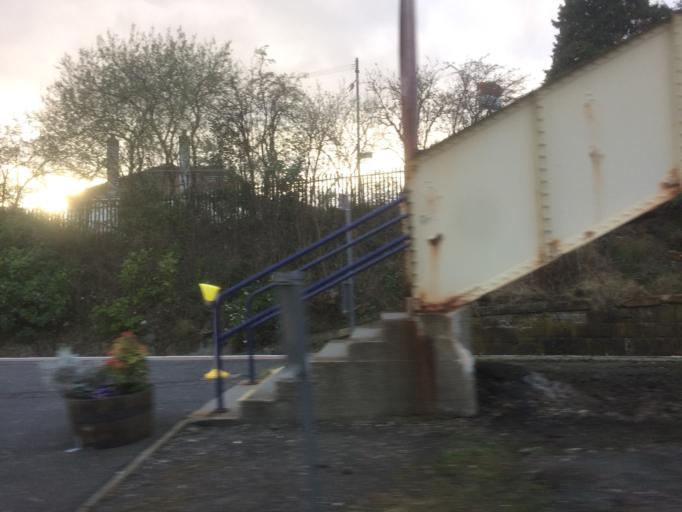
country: GB
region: Scotland
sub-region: East Renfrewshire
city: Giffnock
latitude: 55.8106
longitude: -4.2733
